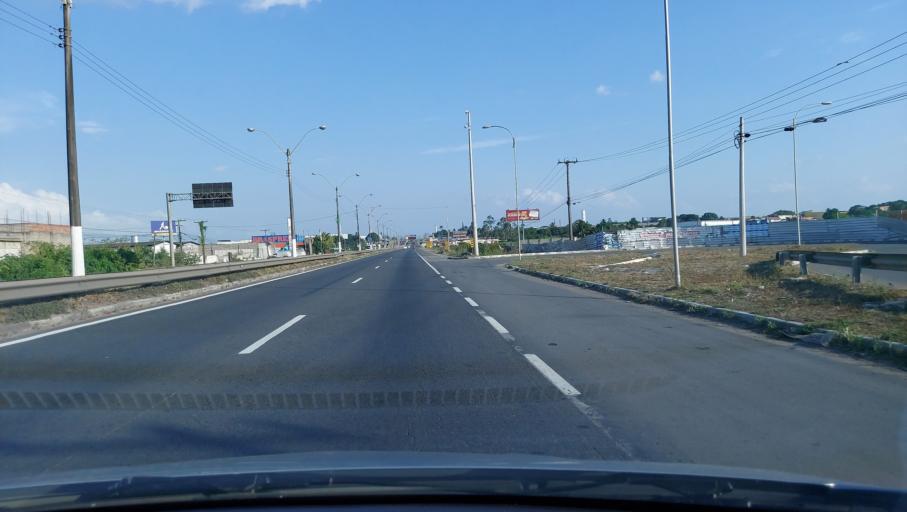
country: BR
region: Bahia
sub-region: Feira De Santana
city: Feira de Santana
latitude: -12.2756
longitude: -38.9313
